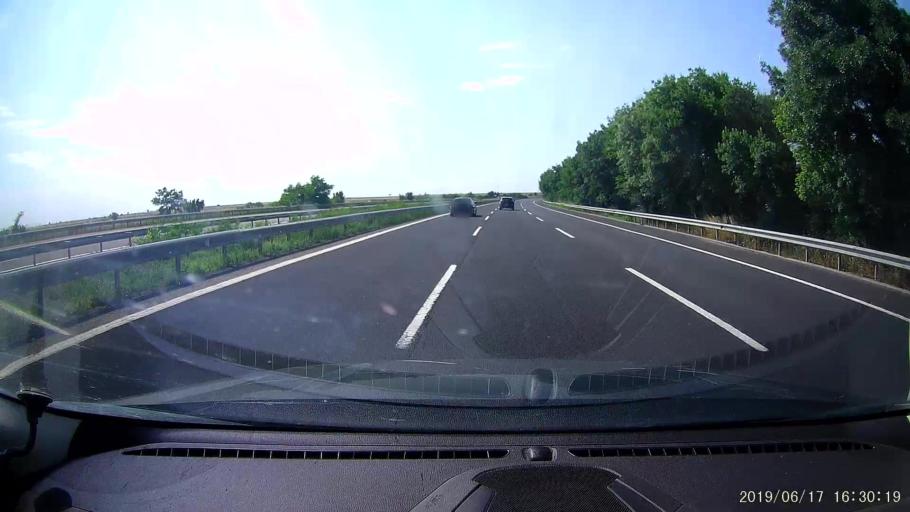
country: TR
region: Tekirdag
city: Beyazkoy
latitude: 41.3445
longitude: 27.6572
